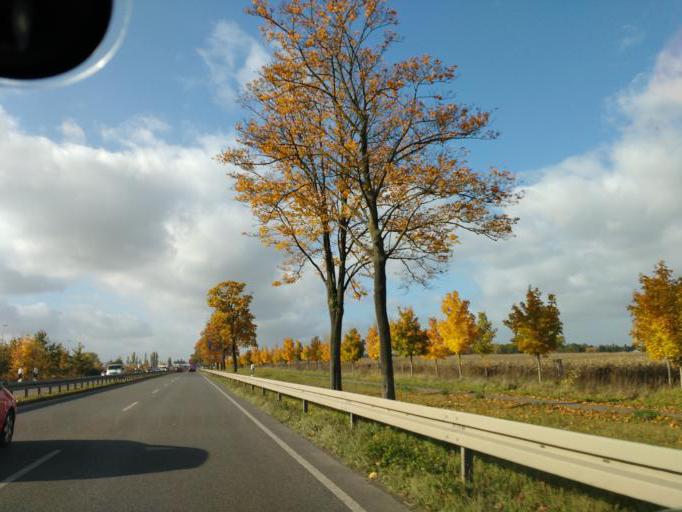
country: DE
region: Brandenburg
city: Petershagen
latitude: 52.4958
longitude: 13.7655
